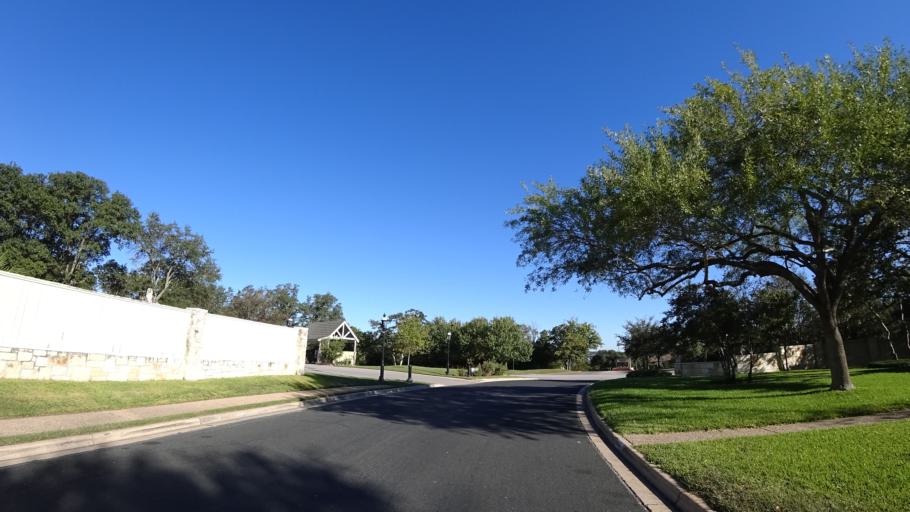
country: US
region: Texas
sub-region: Travis County
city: West Lake Hills
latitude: 30.3342
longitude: -97.8051
